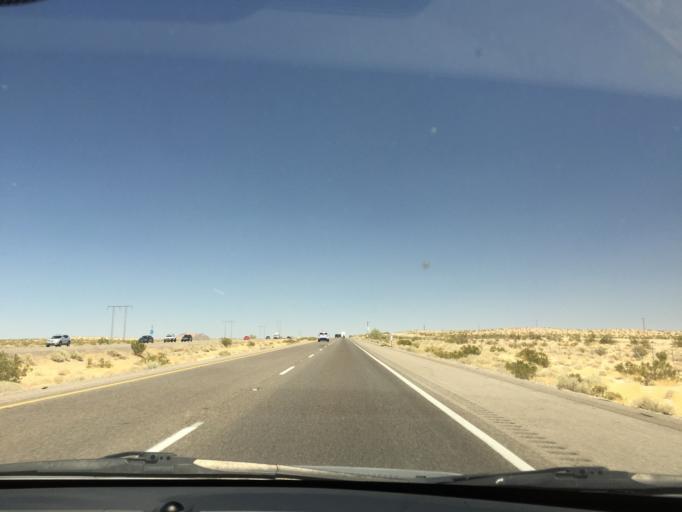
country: US
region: California
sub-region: San Bernardino County
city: Fort Irwin
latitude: 35.0065
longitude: -116.5432
